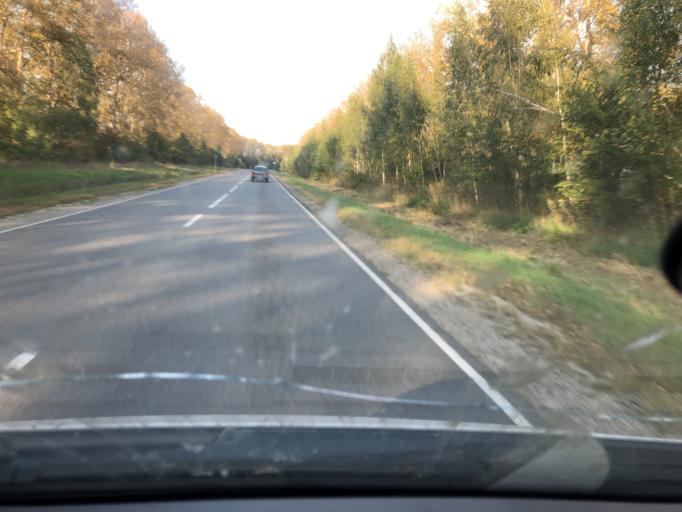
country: RU
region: Kaluga
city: Peremyshl'
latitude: 54.2398
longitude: 36.0728
